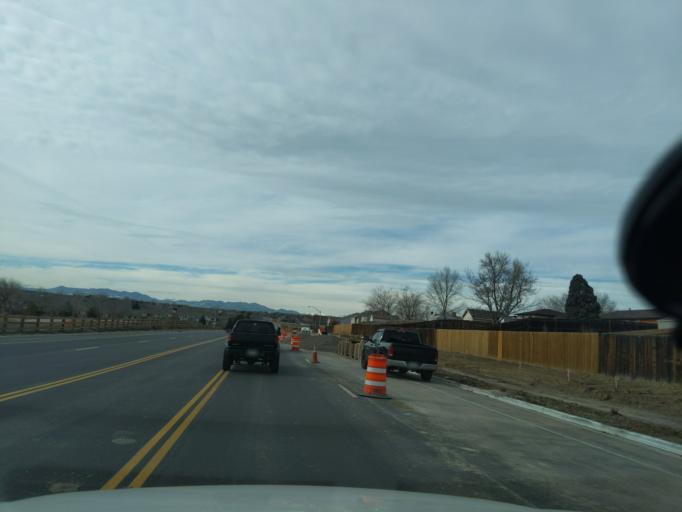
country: US
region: Colorado
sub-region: Adams County
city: Thornton
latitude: 39.8994
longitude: -104.9462
